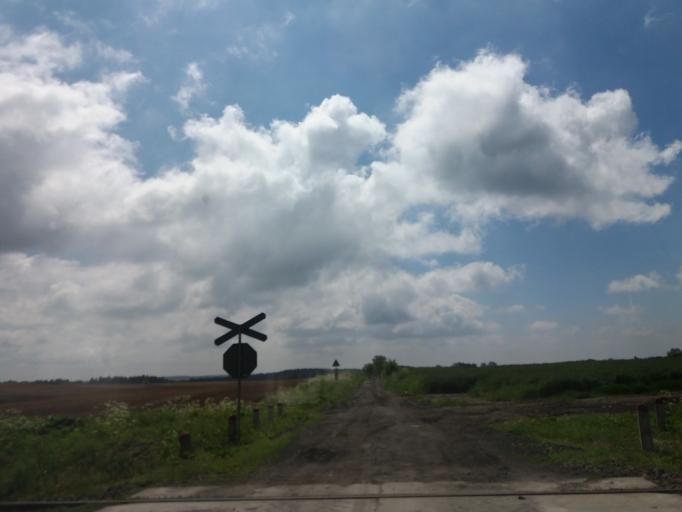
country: PL
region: West Pomeranian Voivodeship
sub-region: Powiat choszczenski
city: Recz
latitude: 53.2820
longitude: 15.5378
